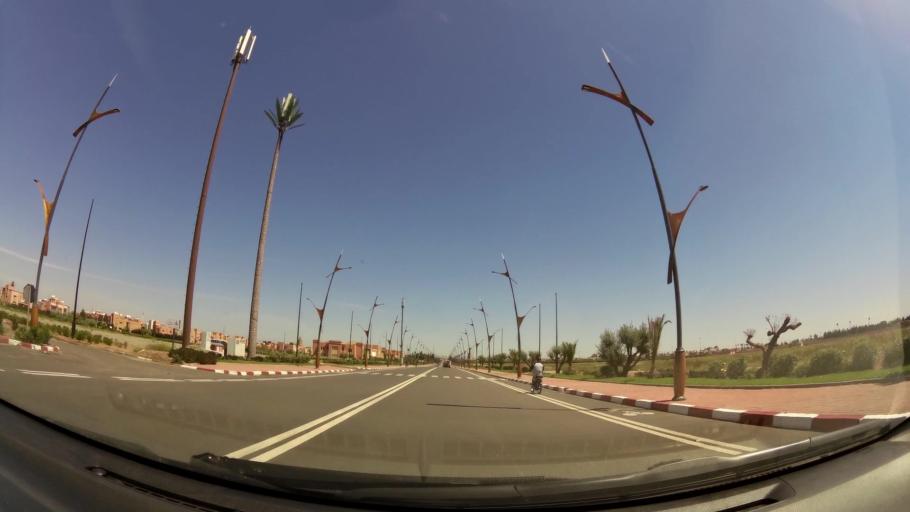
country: MA
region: Marrakech-Tensift-Al Haouz
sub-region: Marrakech
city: Marrakesh
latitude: 31.6077
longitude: -7.9966
